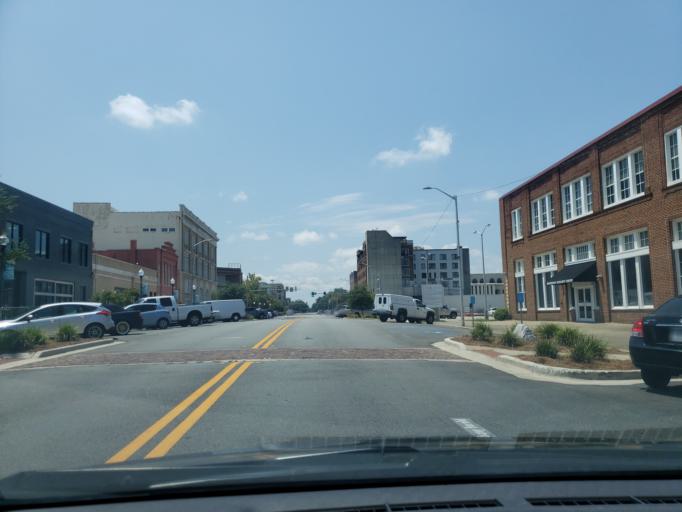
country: US
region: Georgia
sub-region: Dougherty County
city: Albany
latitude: 31.5785
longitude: -84.1500
